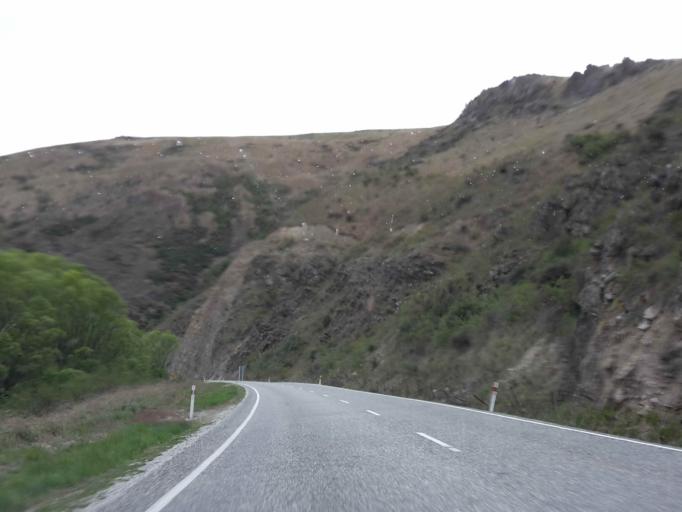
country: NZ
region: Otago
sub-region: Queenstown-Lakes District
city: Wanaka
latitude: -44.6918
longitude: 169.4869
